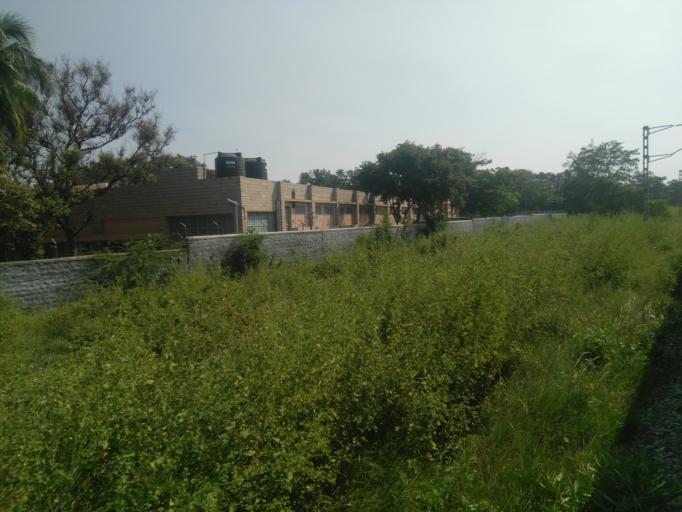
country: IN
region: Tamil Nadu
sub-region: Coimbatore
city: Periyanayakkanpalaiyam
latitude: 11.1475
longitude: 76.9495
